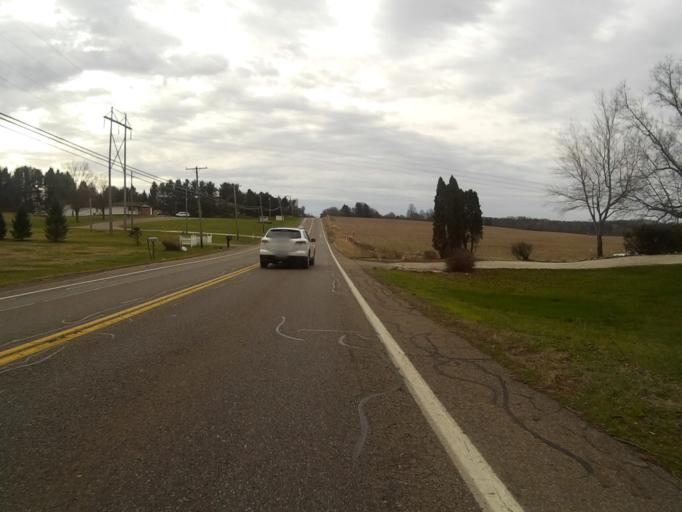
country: US
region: Ohio
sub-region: Portage County
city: Brimfield
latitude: 41.0883
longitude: -81.3466
